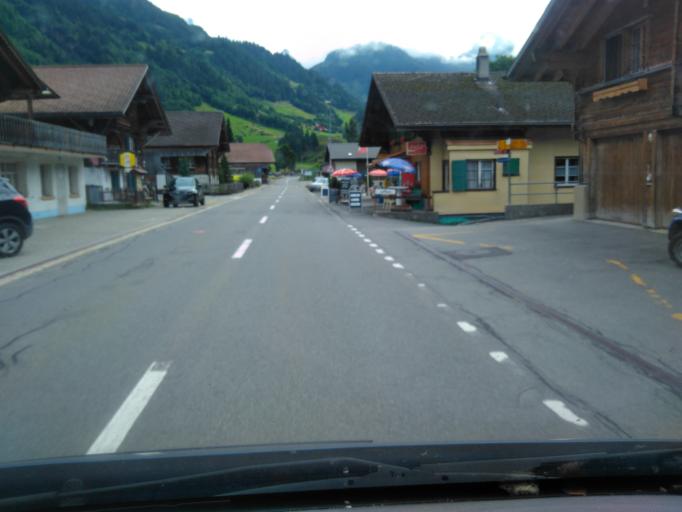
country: CH
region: Obwalden
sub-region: Obwalden
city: Engelberg
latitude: 46.7375
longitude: 8.3515
